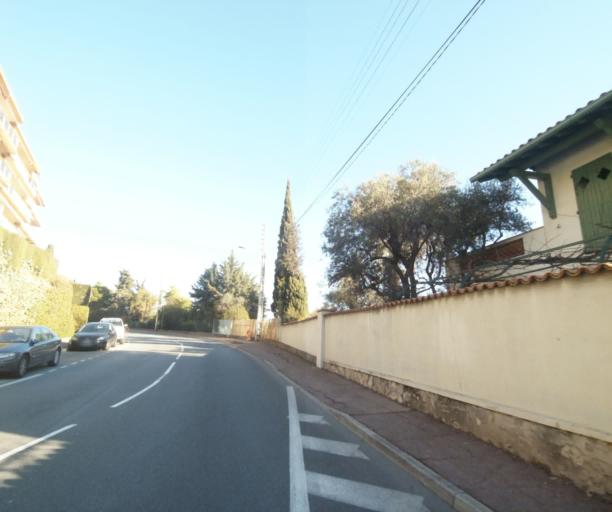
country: FR
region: Provence-Alpes-Cote d'Azur
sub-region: Departement des Alpes-Maritimes
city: Antibes
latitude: 43.5820
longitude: 7.1100
